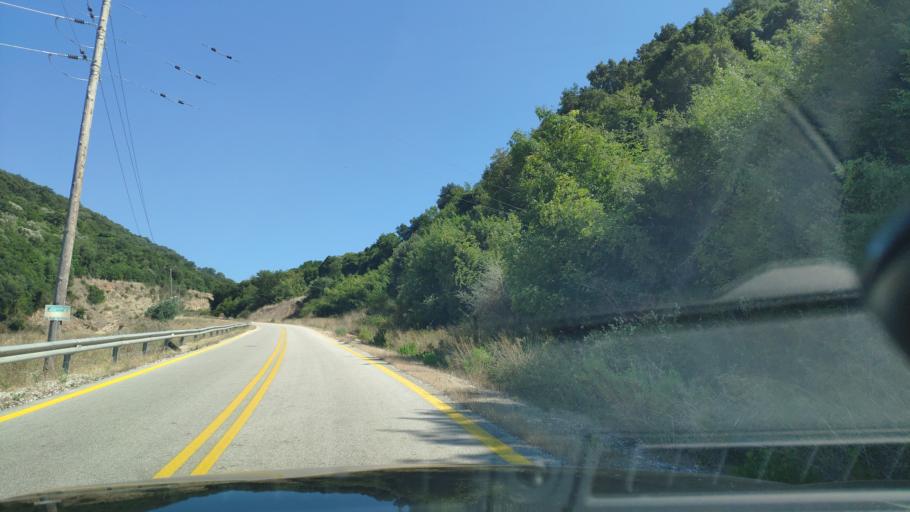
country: GR
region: West Greece
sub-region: Nomos Aitolias kai Akarnanias
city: Amfilochia
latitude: 38.8606
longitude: 21.0827
